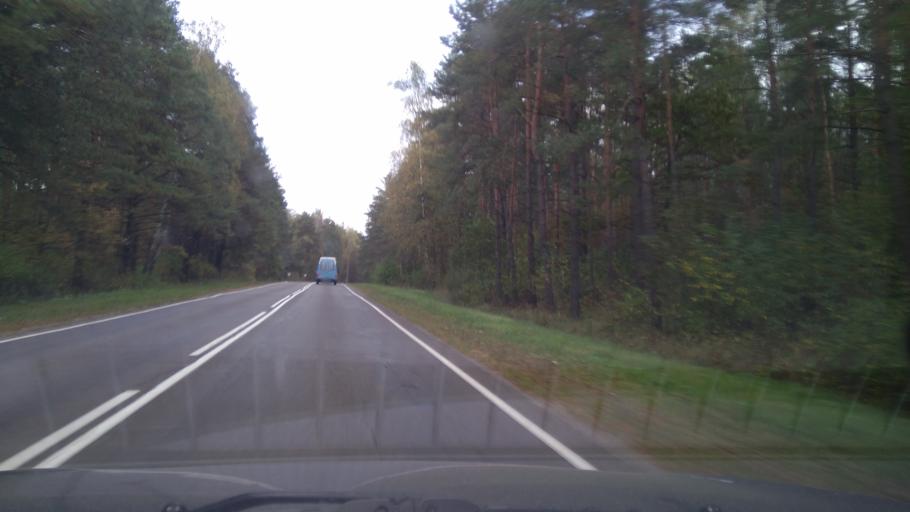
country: BY
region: Minsk
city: Druzhny
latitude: 53.6378
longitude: 27.8994
